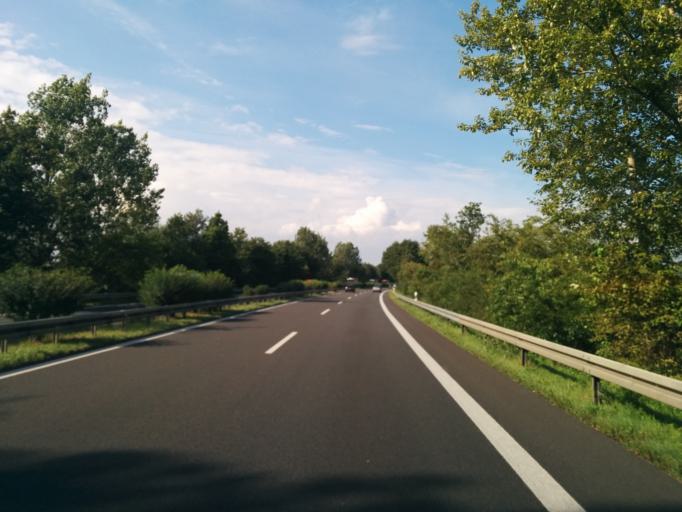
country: DE
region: Brandenburg
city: Gross Kreutz
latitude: 52.3796
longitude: 12.8174
